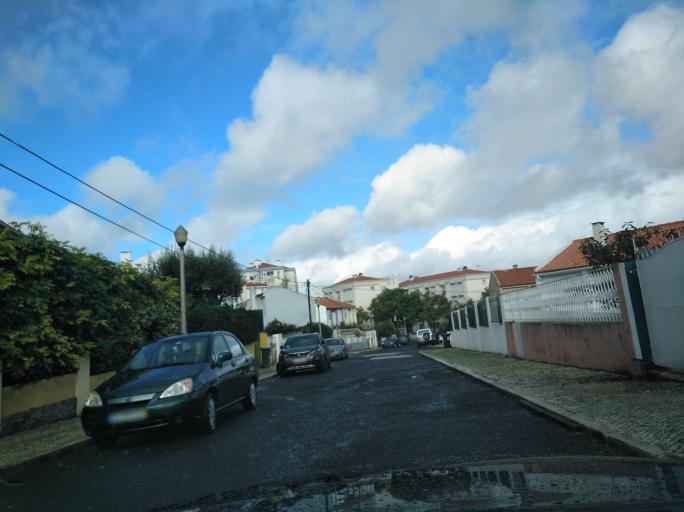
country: PT
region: Lisbon
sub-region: Loures
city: Moscavide
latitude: 38.7584
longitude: -9.1051
